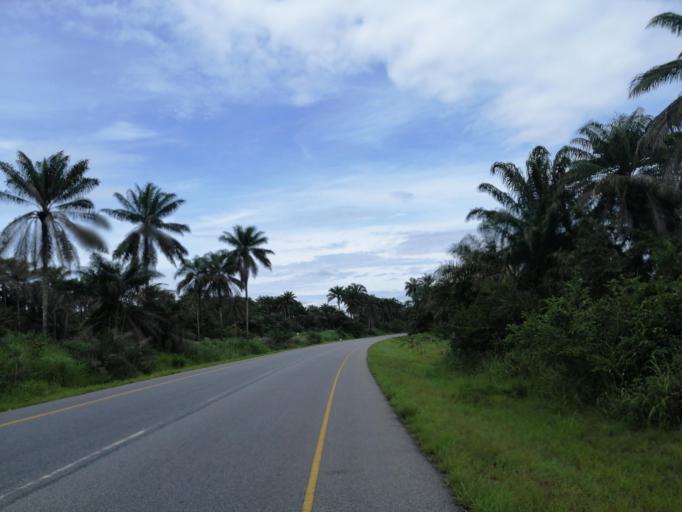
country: SL
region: Northern Province
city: Port Loko
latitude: 8.7595
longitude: -12.9104
